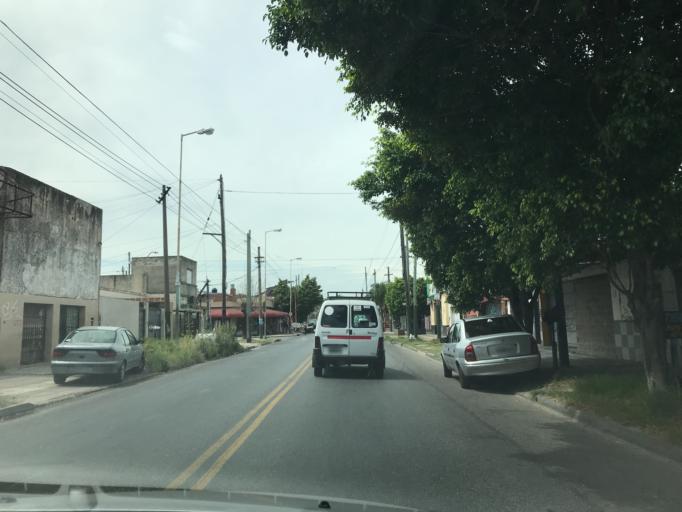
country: AR
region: Buenos Aires
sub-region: Partido de Lomas de Zamora
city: Lomas de Zamora
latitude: -34.7311
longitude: -58.4147
